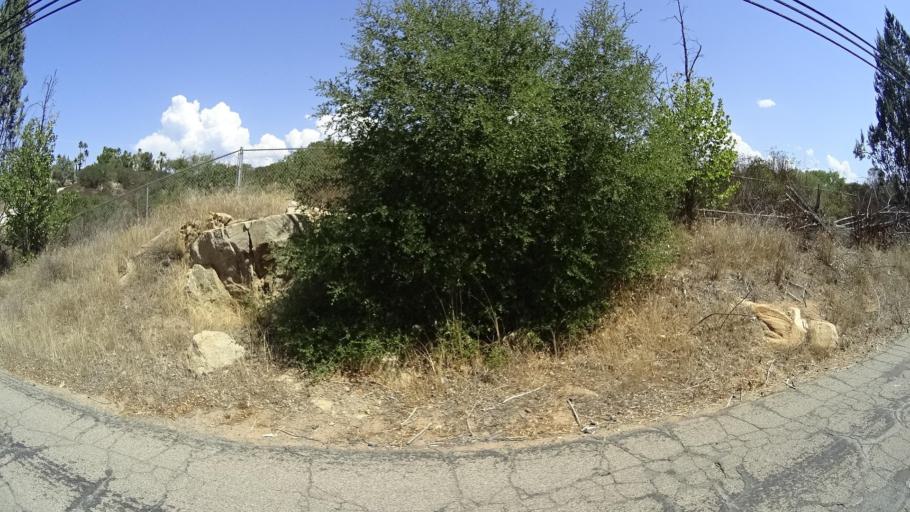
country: US
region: California
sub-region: San Diego County
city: Valley Center
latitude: 33.2244
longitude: -117.0483
